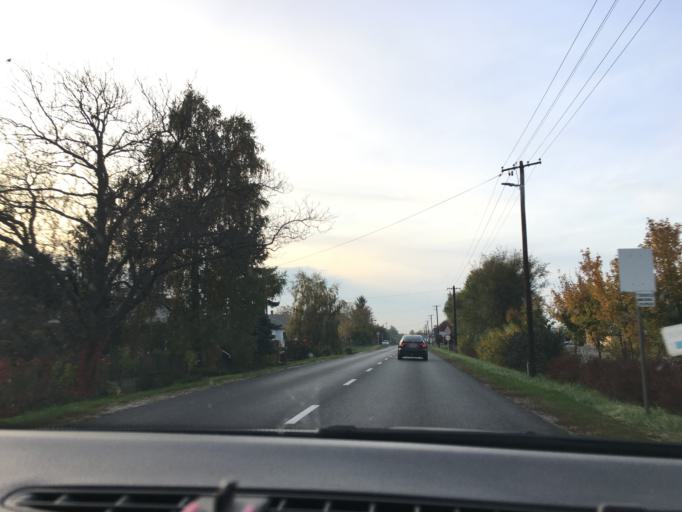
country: HU
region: Szabolcs-Szatmar-Bereg
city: Nagykallo
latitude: 47.8695
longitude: 21.8723
